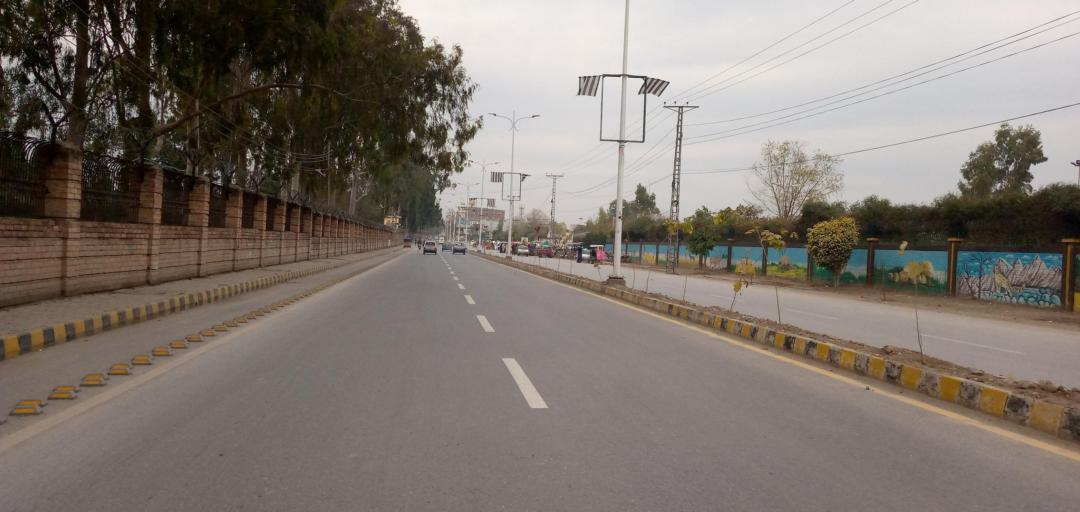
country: PK
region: Khyber Pakhtunkhwa
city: Peshawar
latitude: 34.0154
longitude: 71.4893
